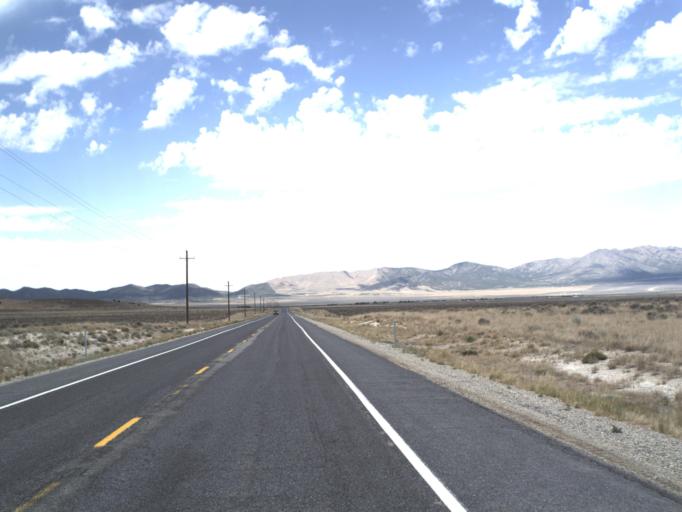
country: US
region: Utah
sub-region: Utah County
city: Eagle Mountain
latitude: 40.0734
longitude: -112.3782
